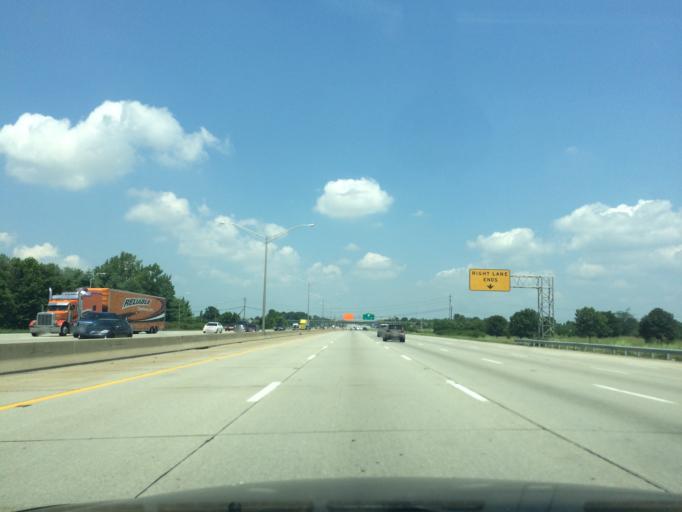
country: US
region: Kentucky
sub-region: Jefferson County
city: Heritage Creek
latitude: 38.1320
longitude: -85.7039
